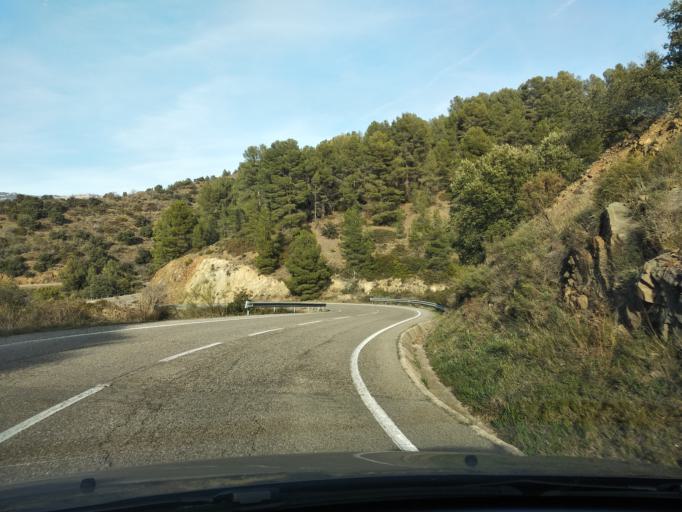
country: ES
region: Catalonia
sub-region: Provincia de Tarragona
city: Falset
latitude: 41.2073
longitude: 0.7750
